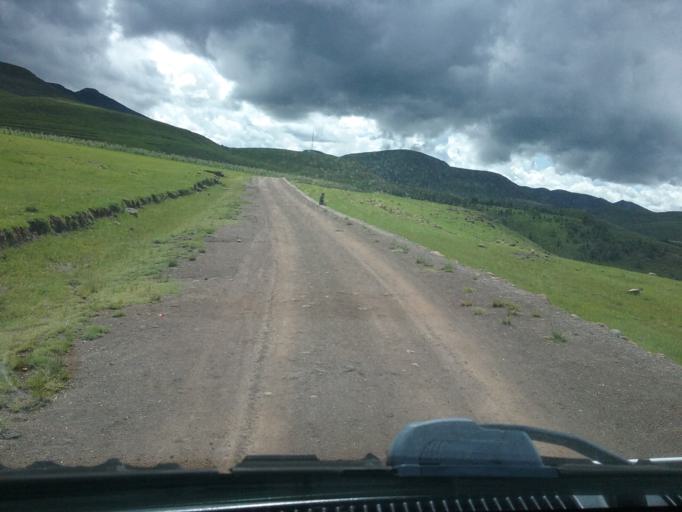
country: LS
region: Maseru
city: Nako
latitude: -29.8784
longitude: 28.0484
